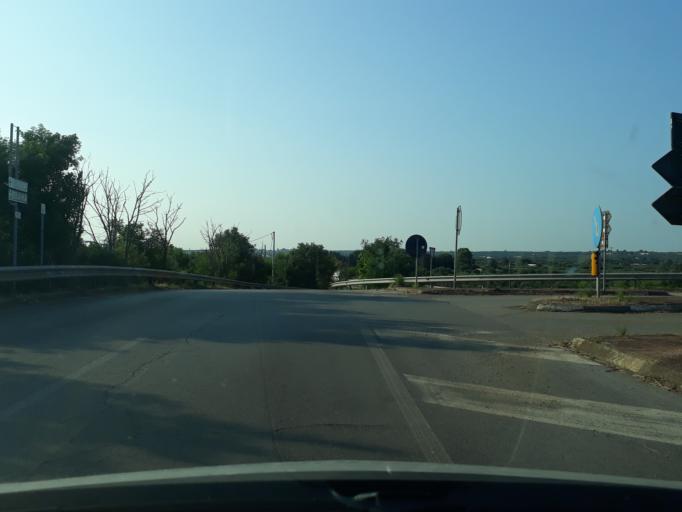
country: IT
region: Apulia
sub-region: Provincia di Brindisi
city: Carovigno
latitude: 40.7414
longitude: 17.7177
